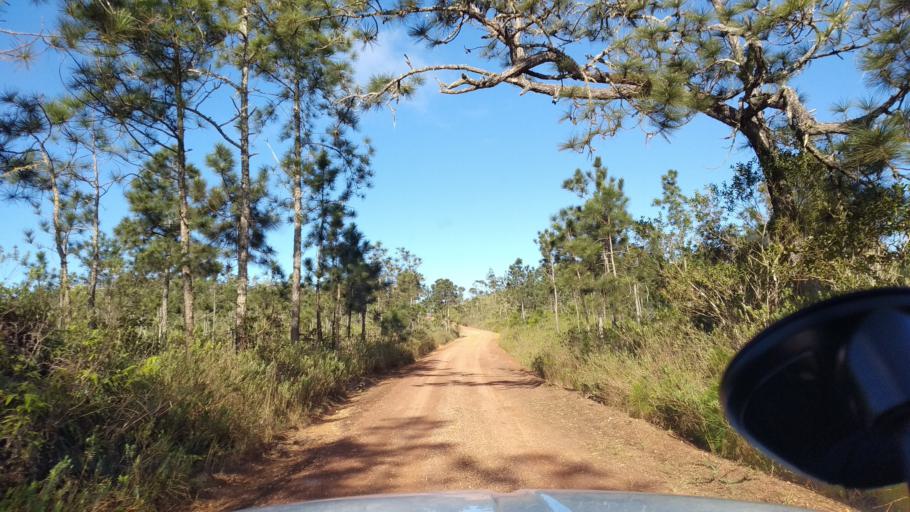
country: BZ
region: Cayo
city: Belmopan
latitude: 16.9980
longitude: -88.8450
